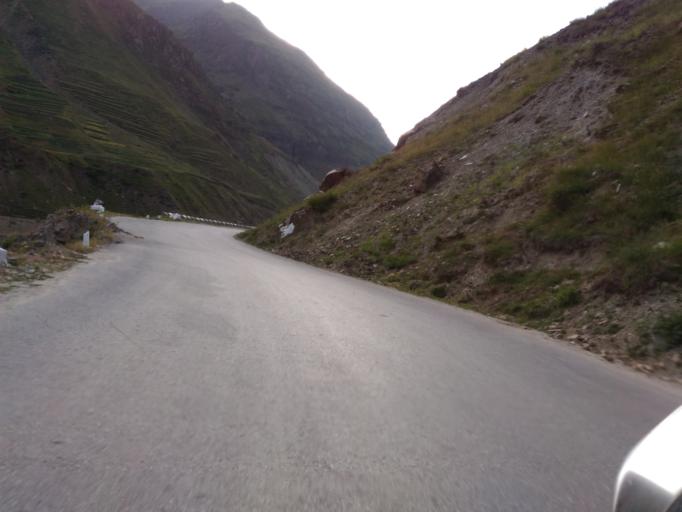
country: IN
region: Himachal Pradesh
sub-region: Lahul and Spiti
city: Kyelang
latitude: 32.4637
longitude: 77.1385
